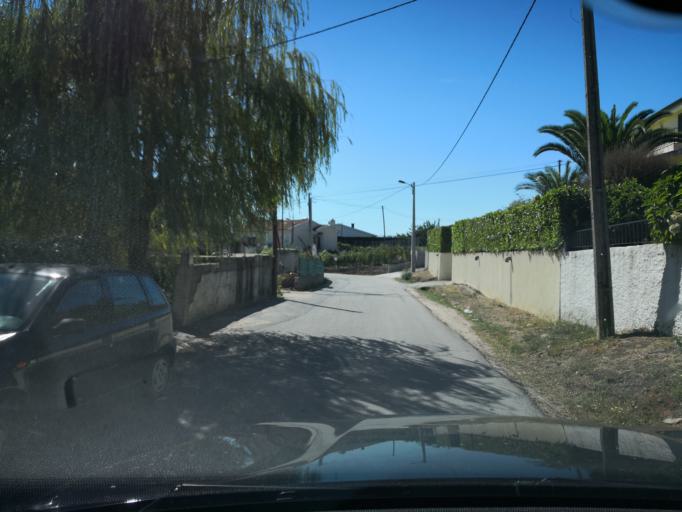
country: PT
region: Vila Real
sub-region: Santa Marta de Penaguiao
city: Santa Marta de Penaguiao
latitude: 41.2566
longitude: -7.7827
